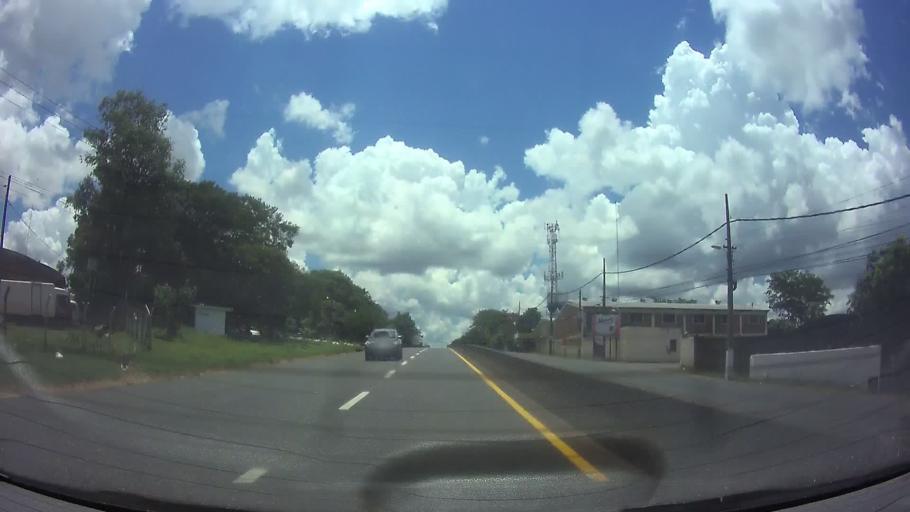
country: PY
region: Central
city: Itaugua
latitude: -25.3818
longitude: -57.3758
